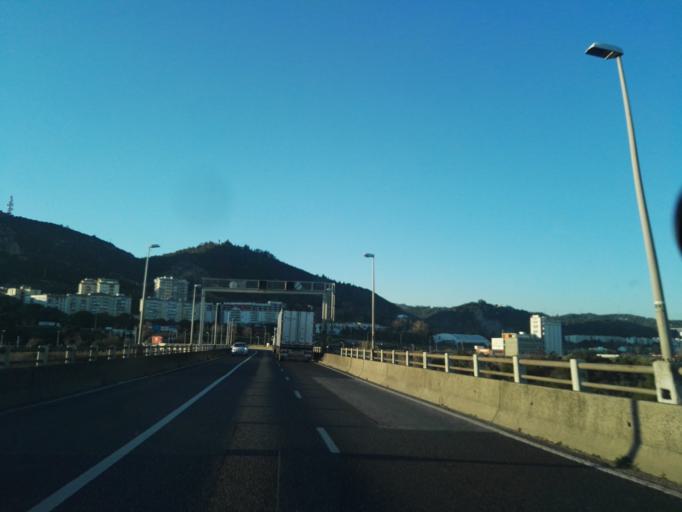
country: PT
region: Lisbon
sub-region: Vila Franca de Xira
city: Vila Franca de Xira
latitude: 38.9591
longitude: -8.9823
